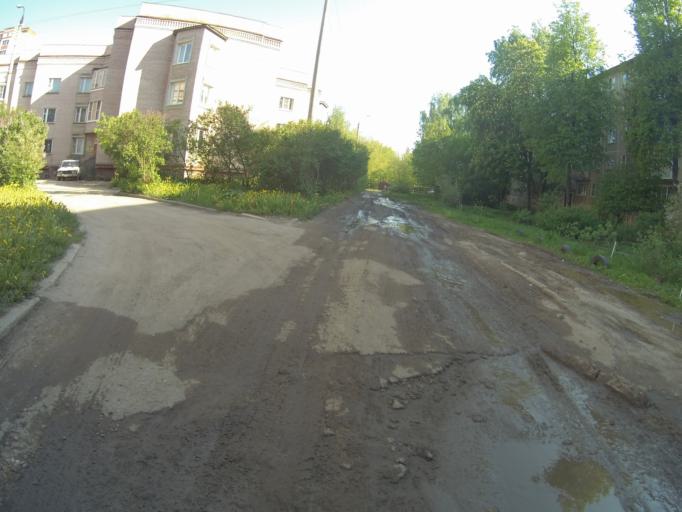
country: RU
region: Vladimir
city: Bogolyubovo
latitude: 56.1741
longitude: 40.4877
